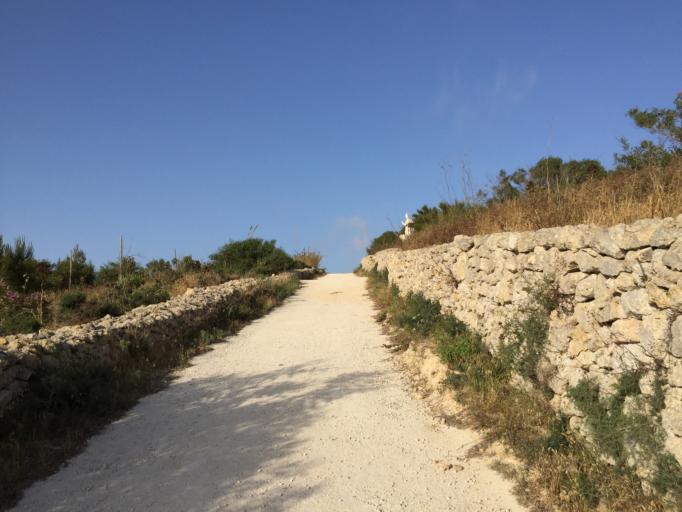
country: MT
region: L-Gharb
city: Gharb
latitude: 36.0603
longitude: 14.2182
